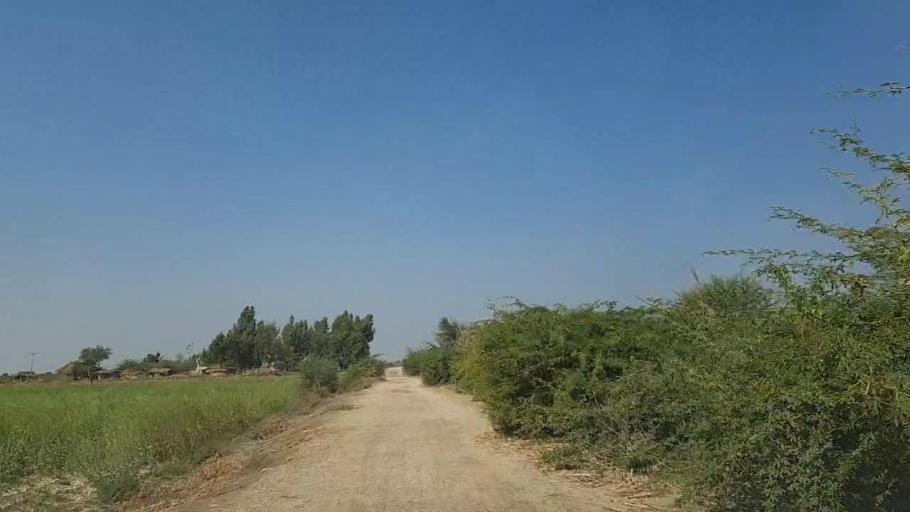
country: PK
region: Sindh
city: Digri
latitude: 25.1907
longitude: 69.1453
